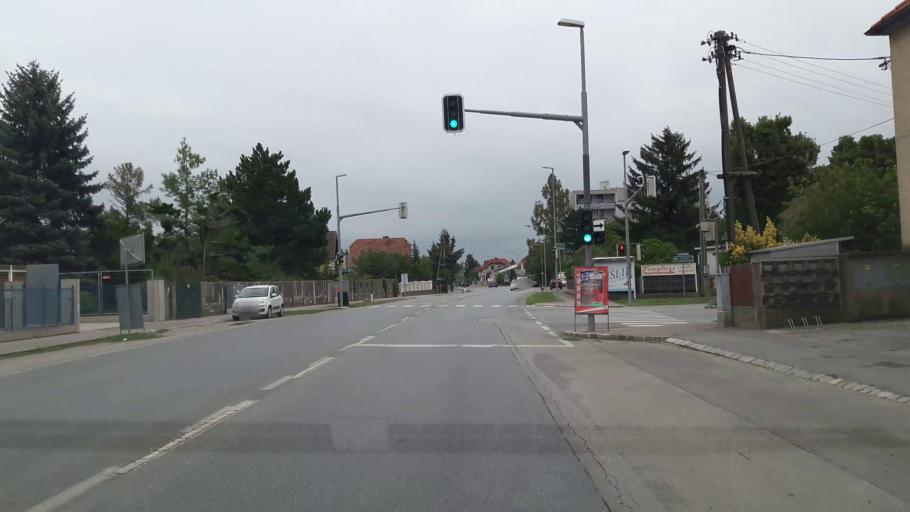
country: AT
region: Lower Austria
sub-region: Politischer Bezirk Ganserndorf
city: Strasshof an der Nordbahn
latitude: 48.3171
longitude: 16.6424
